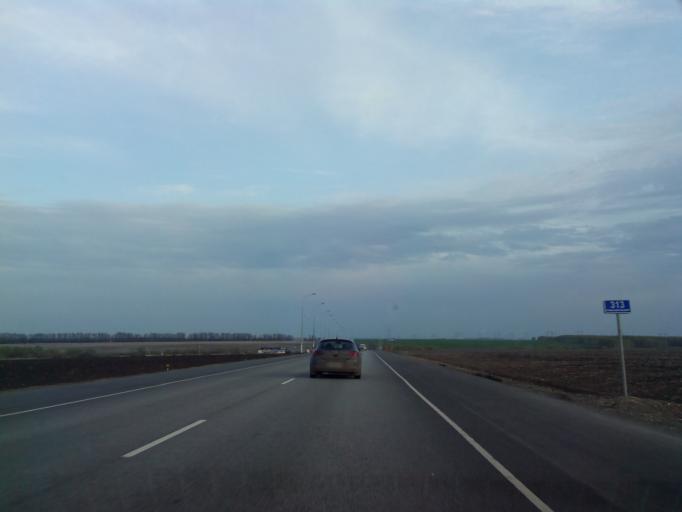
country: RU
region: Rjazan
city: Ryazhsk
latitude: 53.5621
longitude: 40.0508
